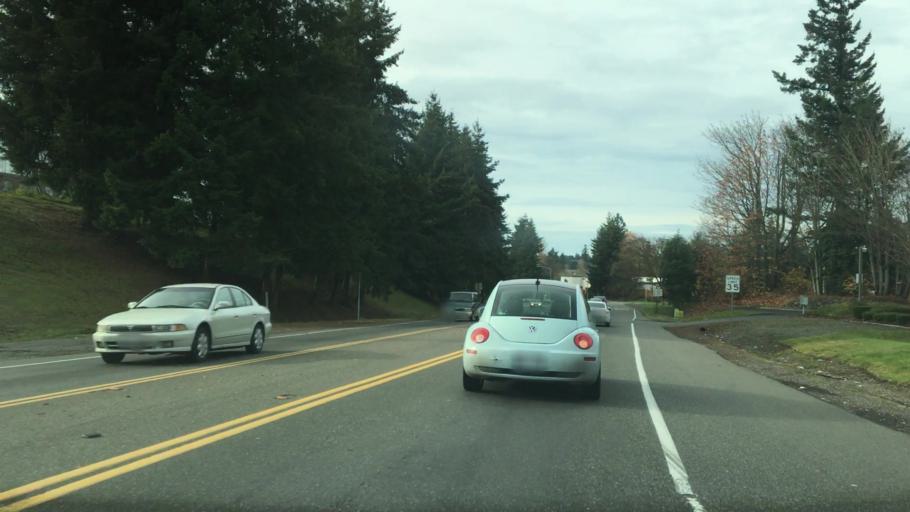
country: US
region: Washington
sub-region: Pierce County
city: Puyallup
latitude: 47.1617
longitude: -122.2990
